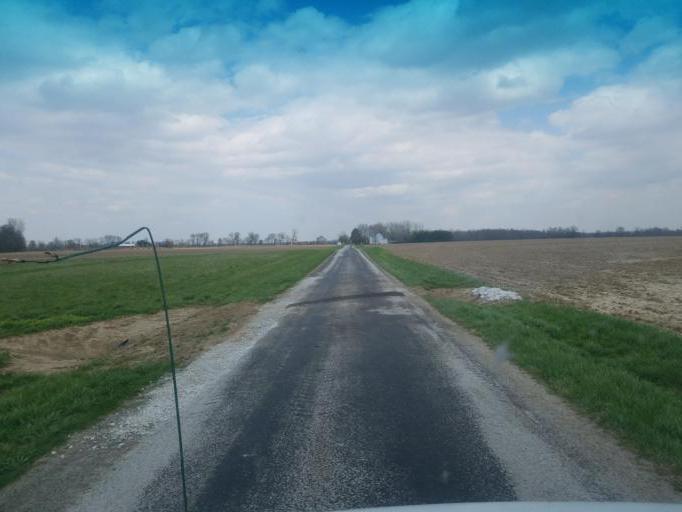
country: US
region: Ohio
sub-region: Wyandot County
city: Upper Sandusky
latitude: 40.9371
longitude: -83.2374
